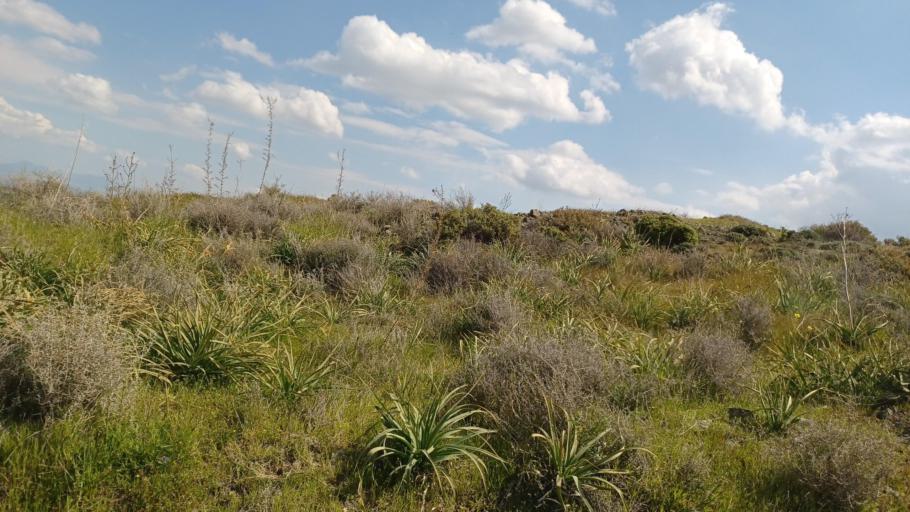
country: CY
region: Lefkosia
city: Lefka
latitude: 35.0801
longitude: 32.9088
